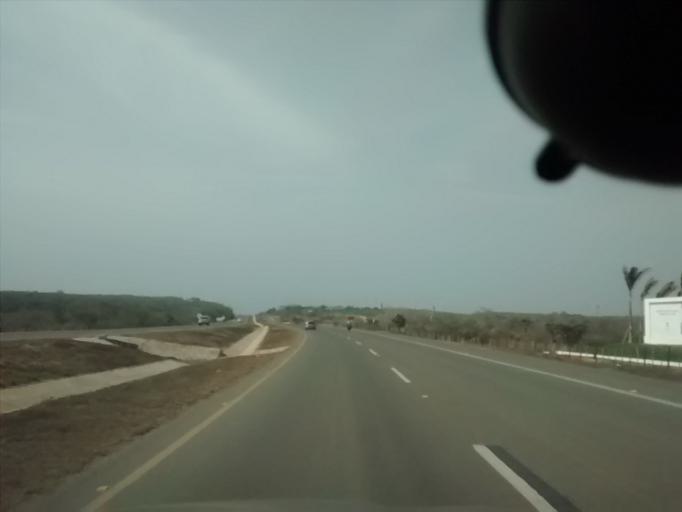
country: CO
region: Bolivar
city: Cartagena
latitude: 10.5026
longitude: -75.4746
